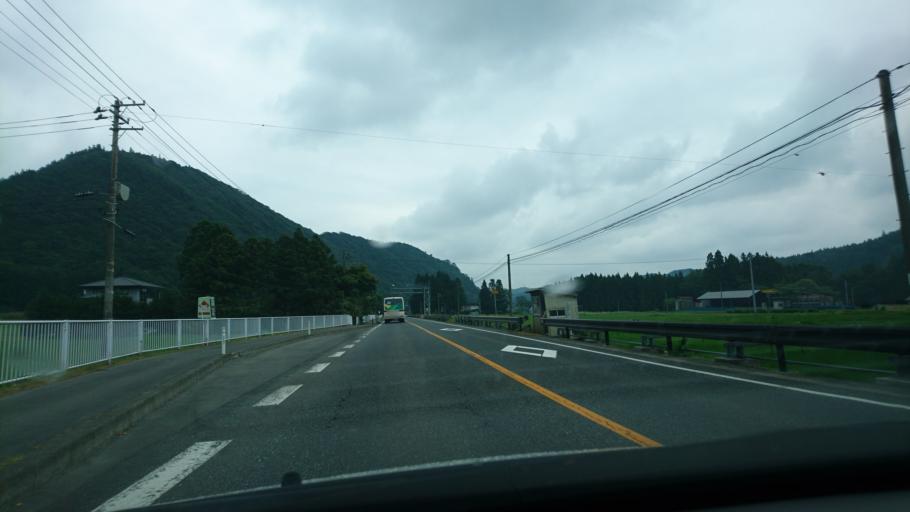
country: JP
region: Miyagi
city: Furukawa
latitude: 38.7266
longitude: 140.7973
